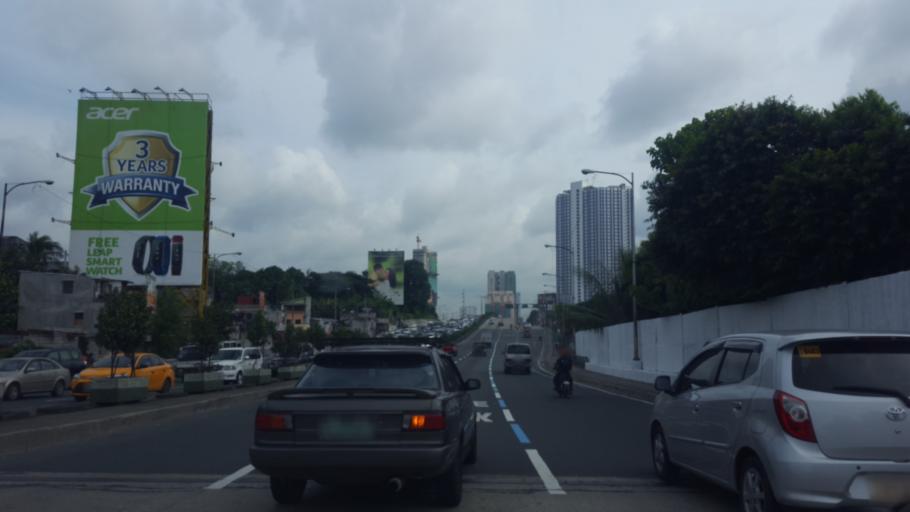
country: PH
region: Metro Manila
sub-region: Marikina
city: Calumpang
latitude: 14.6269
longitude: 121.0743
